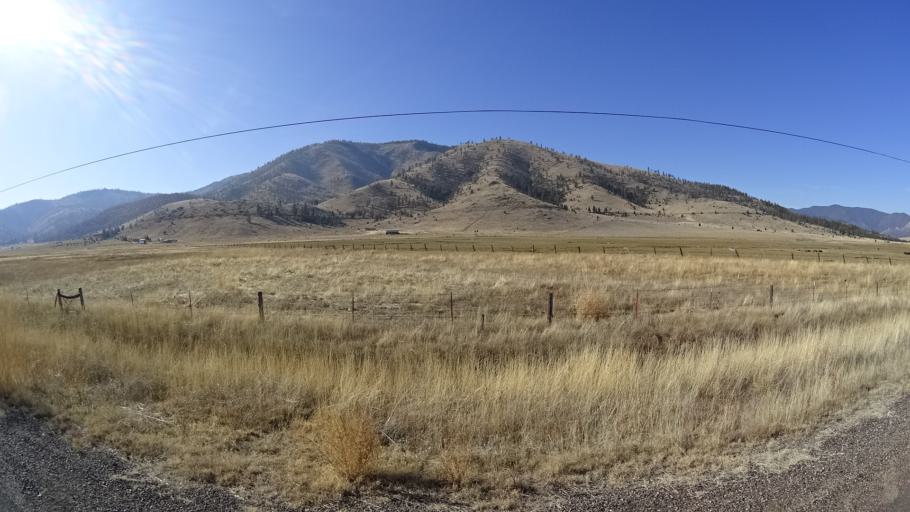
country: US
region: California
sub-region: Siskiyou County
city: Weed
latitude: 41.4858
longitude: -122.4988
